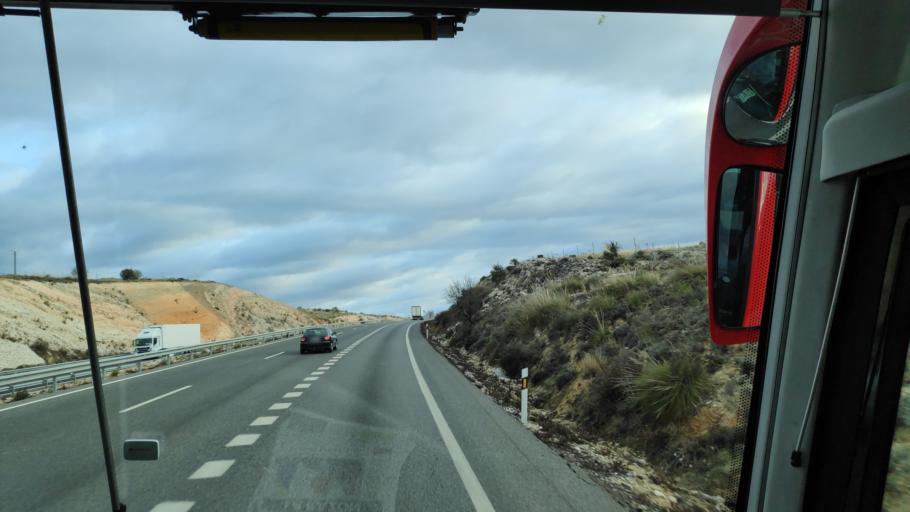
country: ES
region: Madrid
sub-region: Provincia de Madrid
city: Villarejo de Salvanes
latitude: 40.1920
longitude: -3.3007
